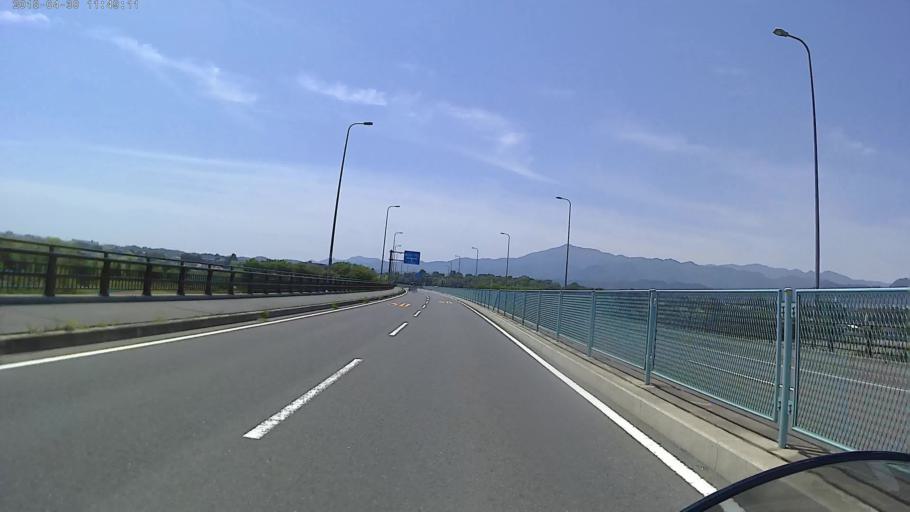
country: JP
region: Kanagawa
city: Zama
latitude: 35.4850
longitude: 139.3576
